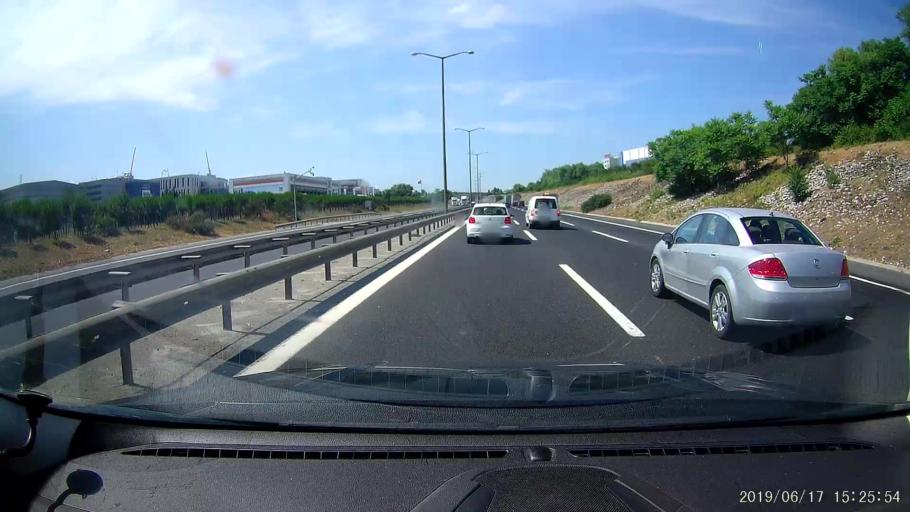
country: TR
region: Istanbul
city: Esenyurt
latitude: 41.0688
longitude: 28.6500
